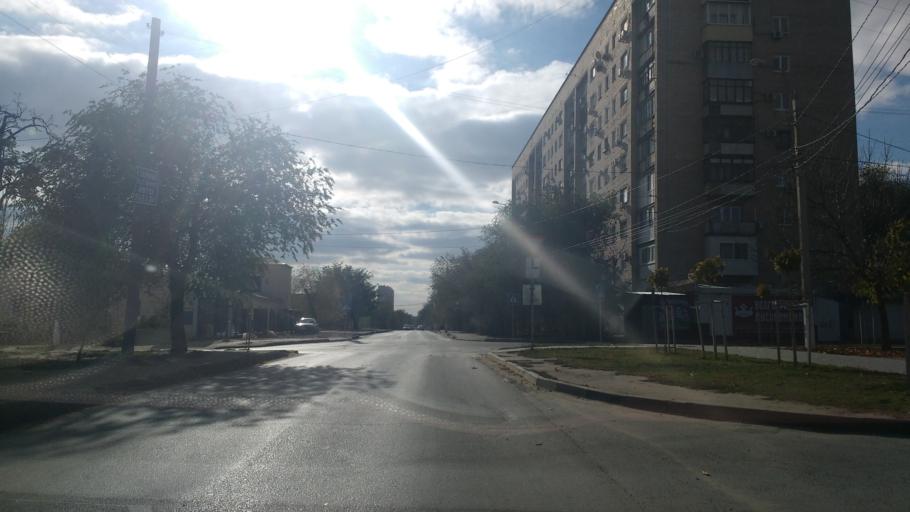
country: RU
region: Volgograd
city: Vodstroy
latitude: 48.7843
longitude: 44.5752
